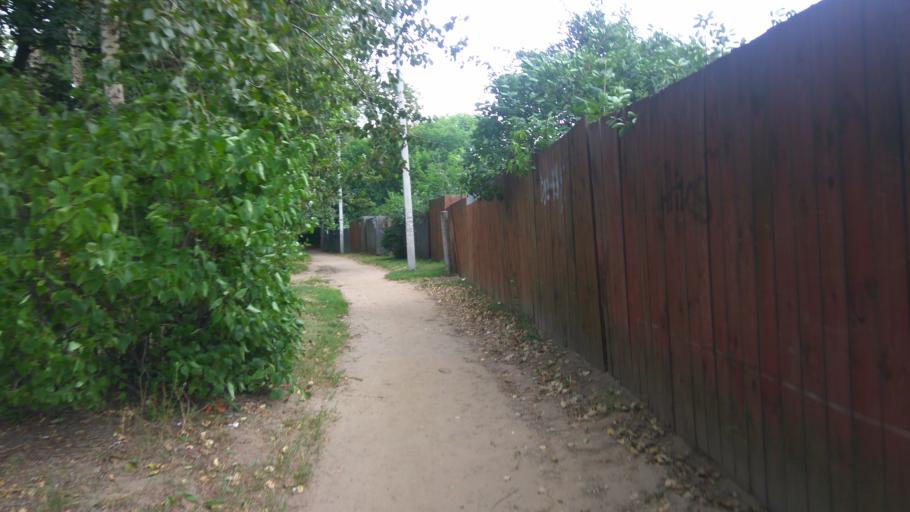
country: RU
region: Moskovskaya
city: Tomilino
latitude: 55.6717
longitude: 37.9335
